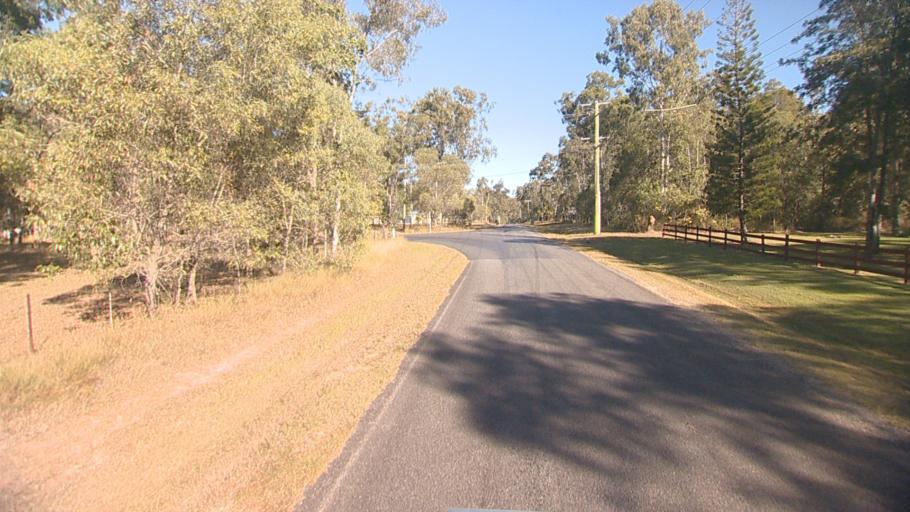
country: AU
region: Queensland
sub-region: Logan
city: Park Ridge South
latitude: -27.7258
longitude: 152.9906
